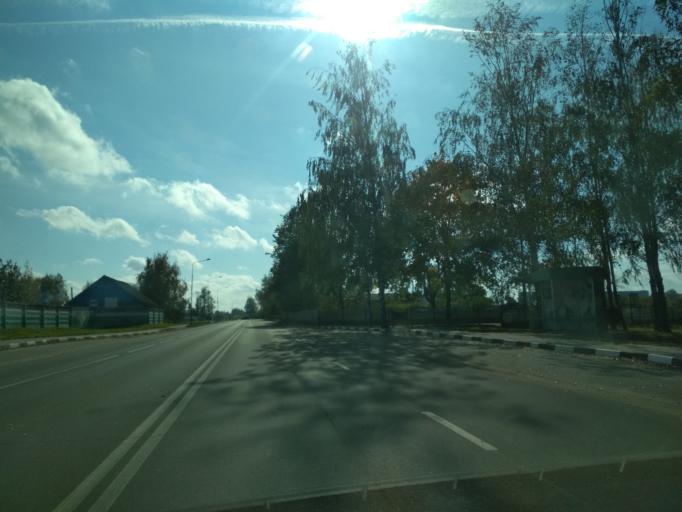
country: BY
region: Minsk
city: Mar''ina Horka
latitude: 53.5018
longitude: 28.1494
